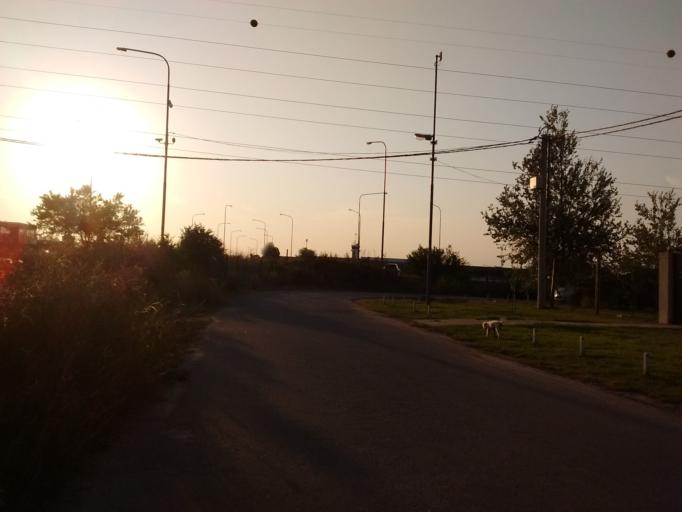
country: AR
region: Santa Fe
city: Funes
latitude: -32.9178
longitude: -60.7760
